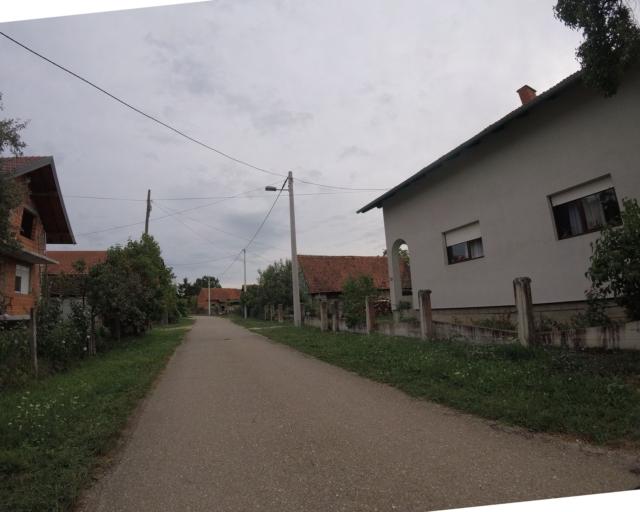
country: HR
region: Zagrebacka
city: Kuce
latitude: 45.7154
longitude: 16.1526
